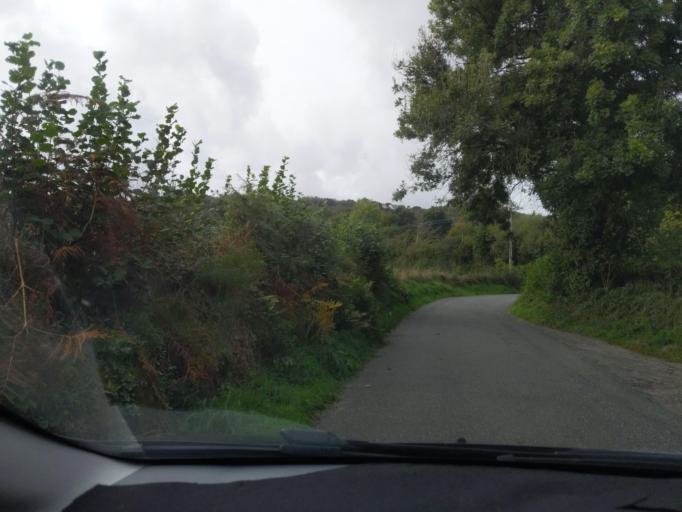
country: GB
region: England
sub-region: Cornwall
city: Lostwithiel
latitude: 50.4013
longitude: -4.6948
